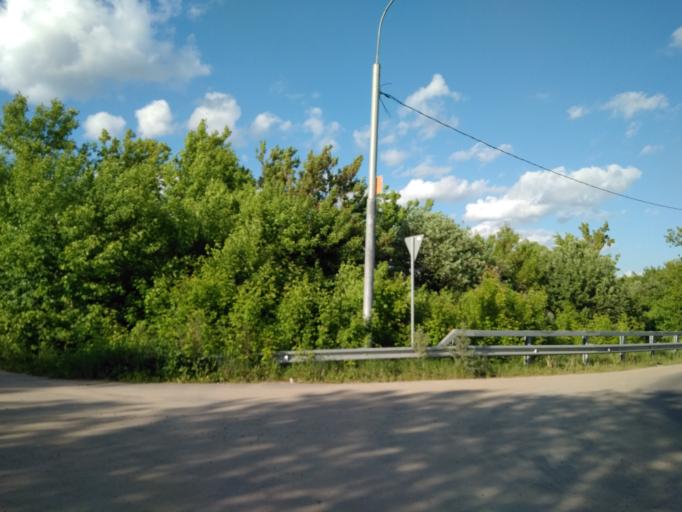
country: RU
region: Moskovskaya
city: Zhukovskiy
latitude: 55.5741
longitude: 38.1043
